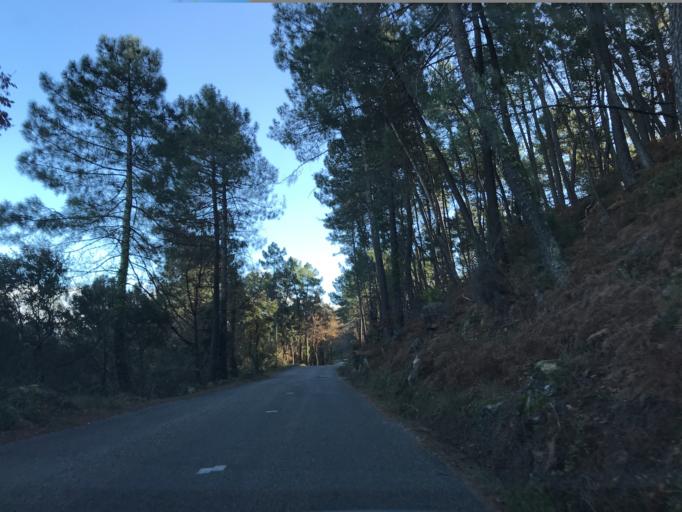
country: FR
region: Rhone-Alpes
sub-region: Departement de l'Ardeche
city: Les Vans
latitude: 44.4126
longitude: 4.0995
